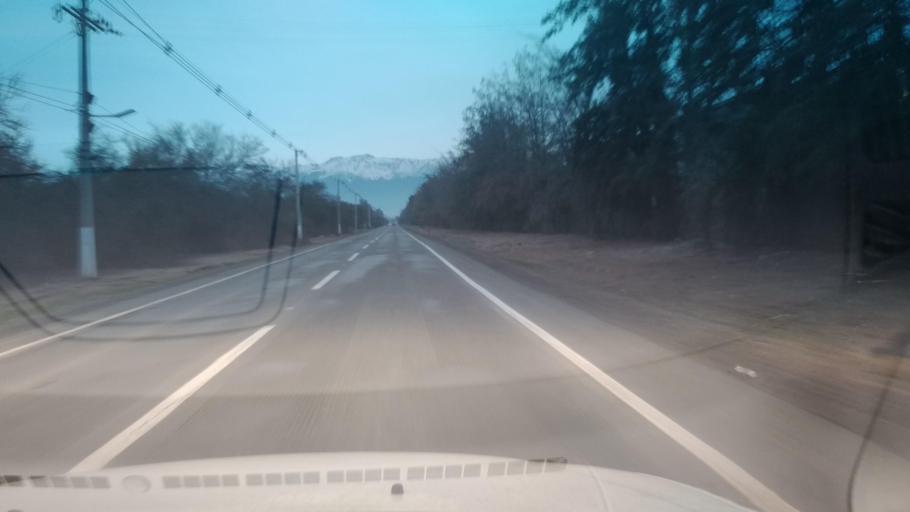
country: CL
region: Santiago Metropolitan
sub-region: Provincia de Chacabuco
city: Chicureo Abajo
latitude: -33.0937
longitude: -70.7091
